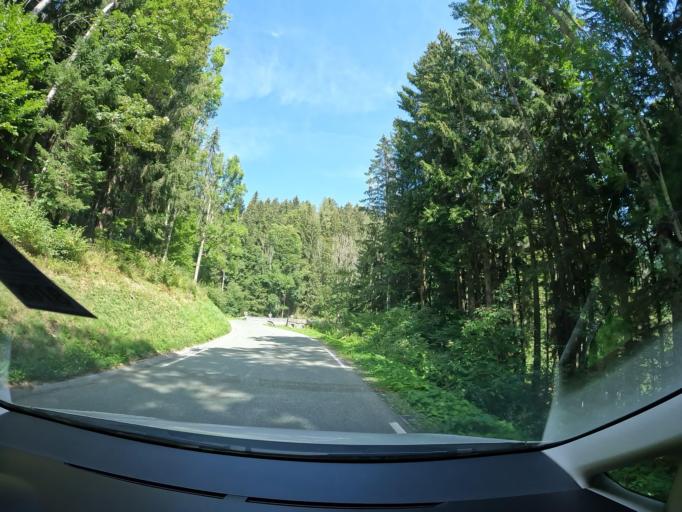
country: AT
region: Carinthia
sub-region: Politischer Bezirk Feldkirchen
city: Glanegg
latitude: 46.7377
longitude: 14.1934
